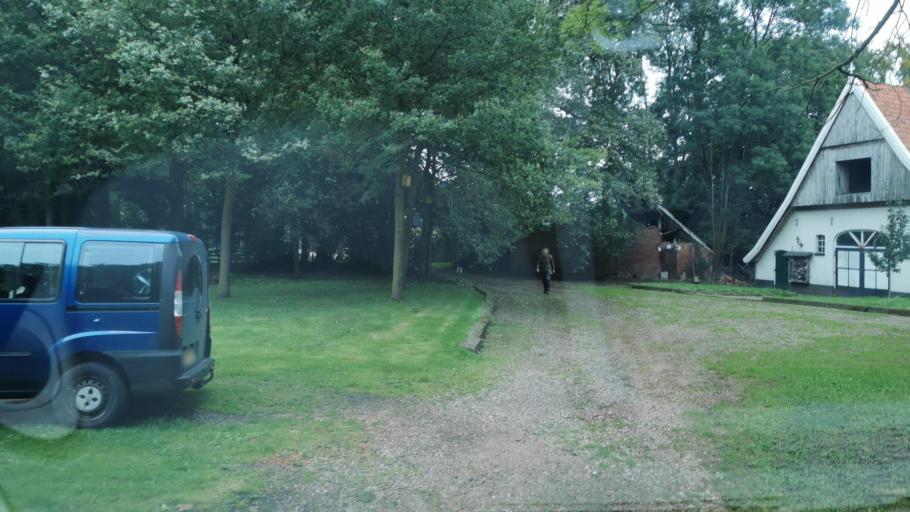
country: NL
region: Overijssel
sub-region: Gemeente Oldenzaal
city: Oldenzaal
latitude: 52.3231
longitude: 6.9468
